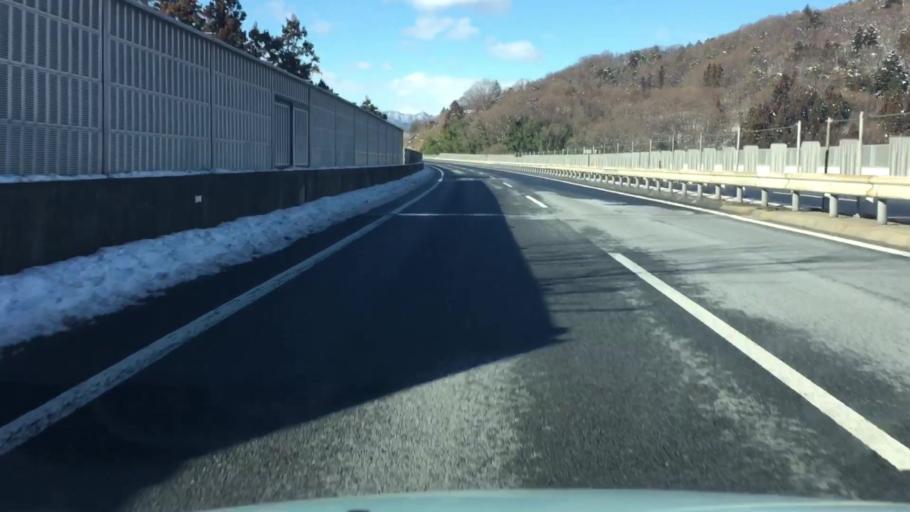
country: JP
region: Gunma
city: Numata
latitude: 36.6722
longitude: 139.0416
